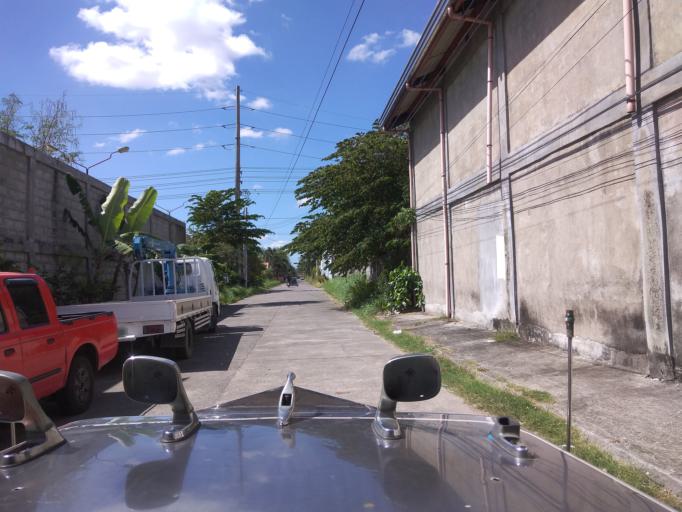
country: PH
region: Central Luzon
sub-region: Province of Pampanga
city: Calibutbut
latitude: 15.1145
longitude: 120.6006
